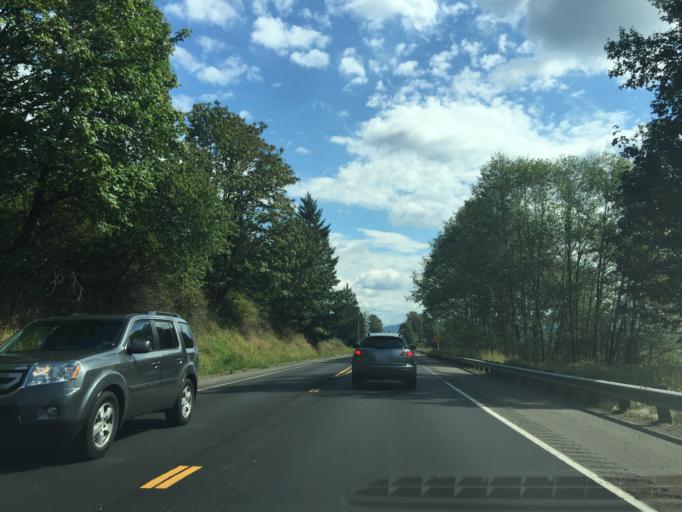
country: US
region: Washington
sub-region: Snohomish County
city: Three Lakes
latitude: 47.9073
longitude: -122.0459
